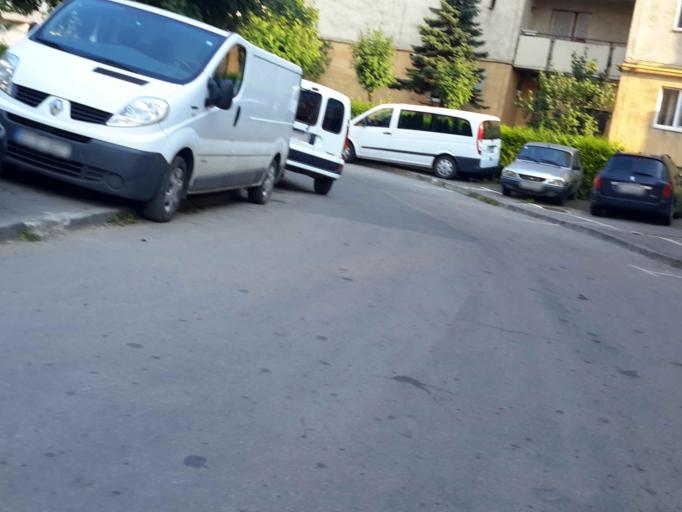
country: RO
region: Cluj
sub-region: Municipiul Cluj-Napoca
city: Cluj-Napoca
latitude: 46.7796
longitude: 23.6039
